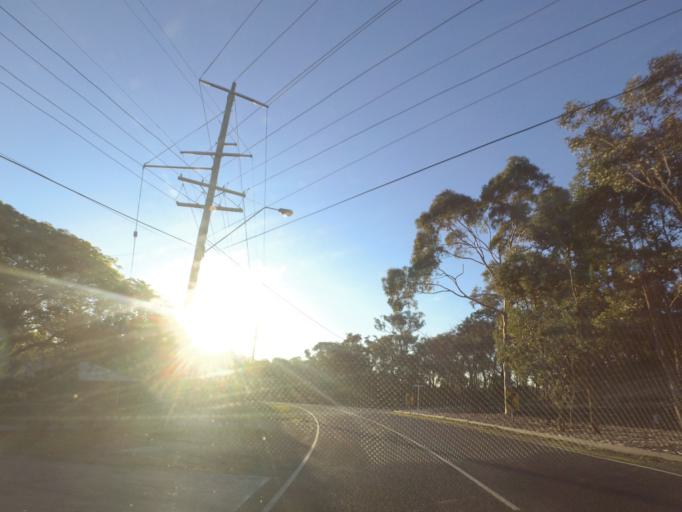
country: AU
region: Victoria
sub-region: Manningham
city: Park Orchards
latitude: -37.7596
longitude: 145.2179
